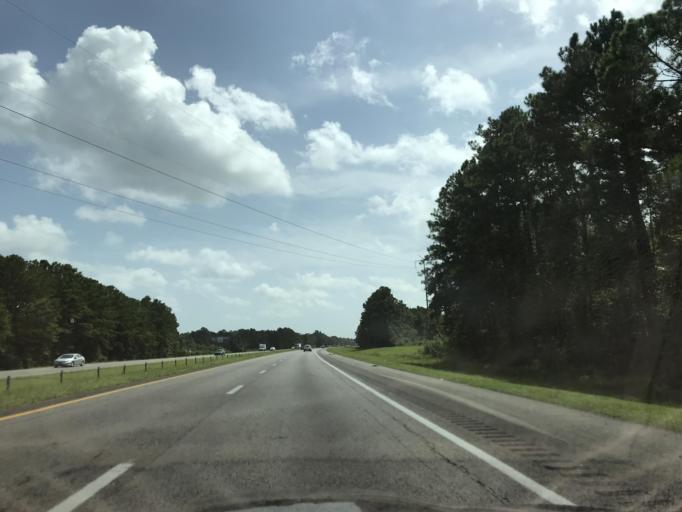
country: US
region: North Carolina
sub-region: Pender County
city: Rocky Point
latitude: 34.4184
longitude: -77.8694
